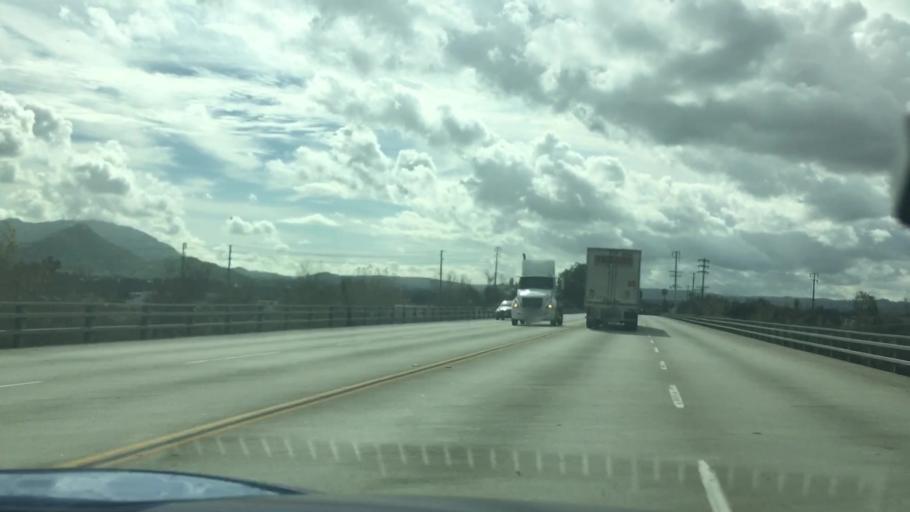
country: US
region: California
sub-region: Riverside County
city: Highgrove
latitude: 34.0257
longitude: -117.3636
